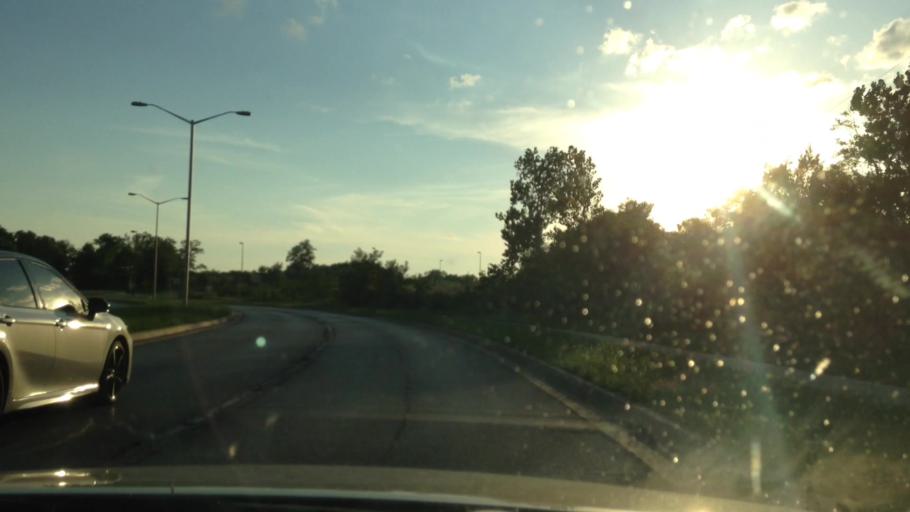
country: US
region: Missouri
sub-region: Clay County
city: Pleasant Valley
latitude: 39.2672
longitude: -94.4873
